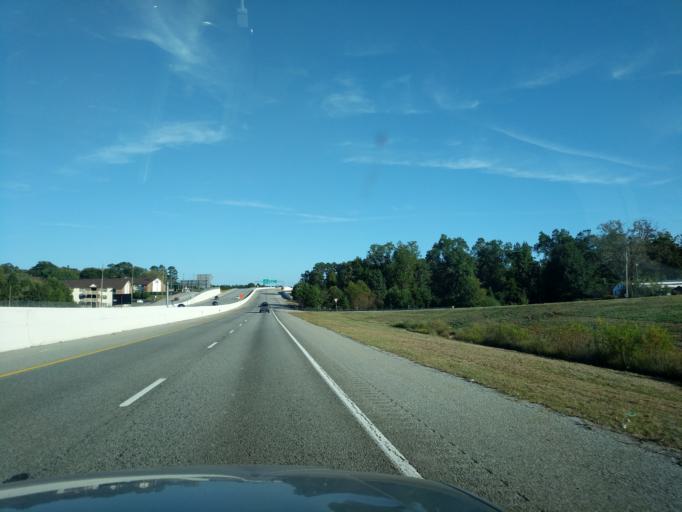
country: US
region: South Carolina
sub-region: Spartanburg County
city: Southern Shops
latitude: 34.9961
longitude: -81.9774
